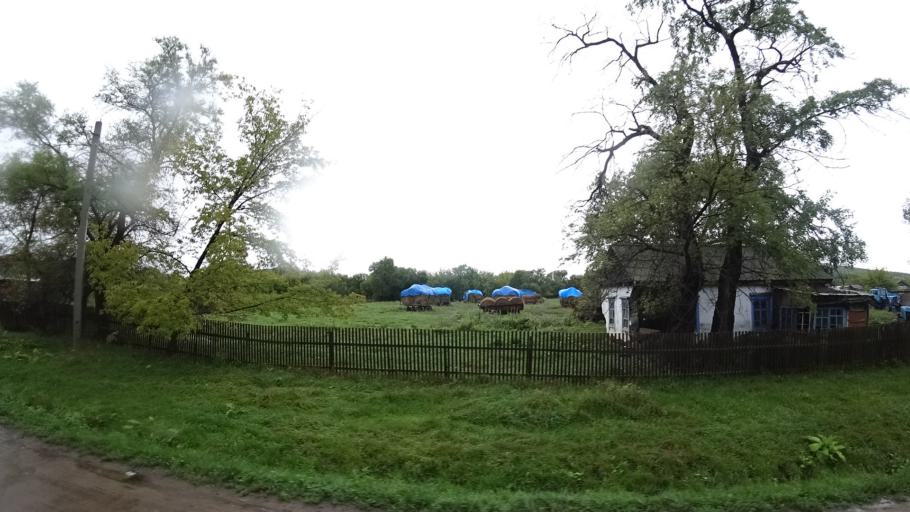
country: RU
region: Primorskiy
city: Monastyrishche
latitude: 44.2541
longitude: 132.4267
